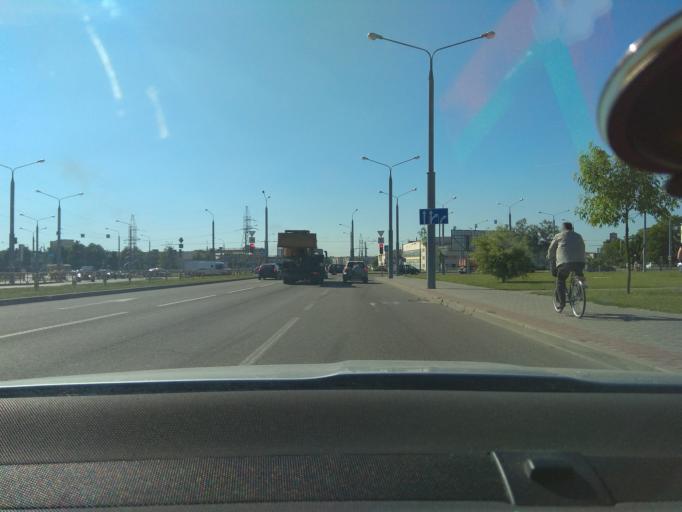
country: BY
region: Grodnenskaya
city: Hrodna
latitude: 53.6525
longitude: 23.7948
